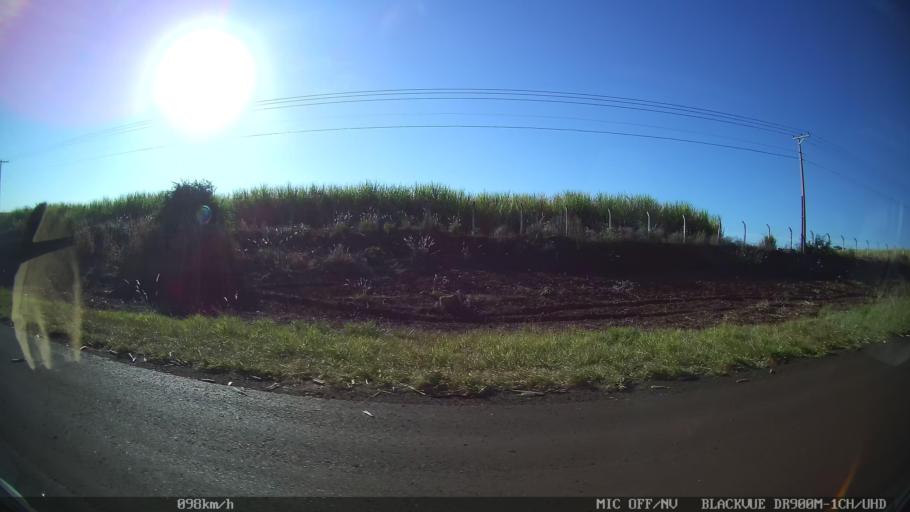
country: BR
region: Sao Paulo
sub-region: Olimpia
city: Olimpia
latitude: -20.7204
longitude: -49.0153
